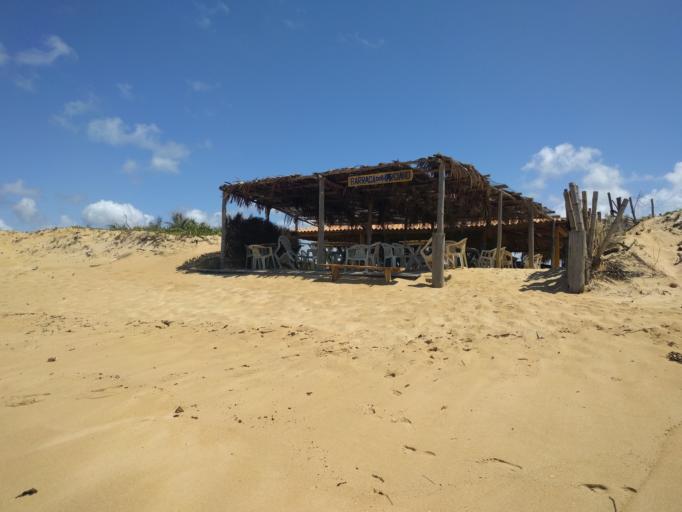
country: BR
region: Espirito Santo
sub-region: Conceicao Da Barra
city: Conceicao da Barra
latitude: -18.4157
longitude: -39.6983
